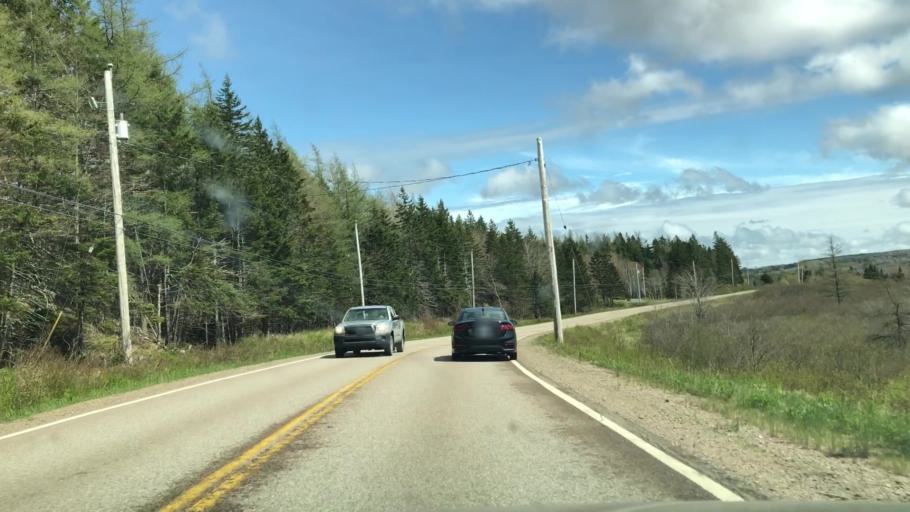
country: CA
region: Nova Scotia
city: Antigonish
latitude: 45.1912
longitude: -61.9909
